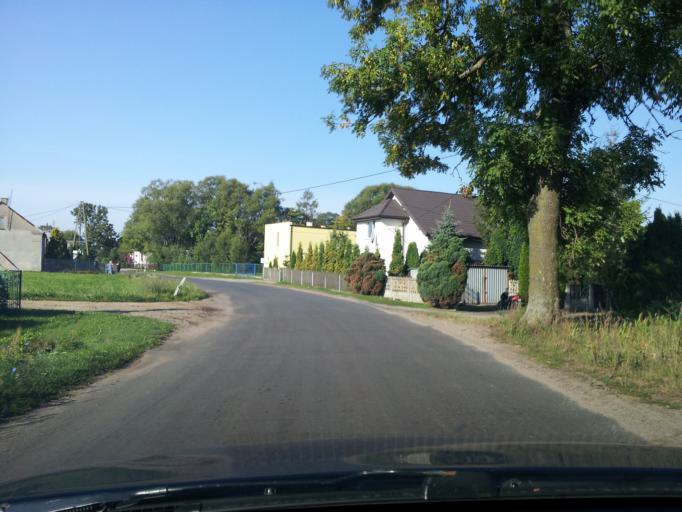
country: PL
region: Kujawsko-Pomorskie
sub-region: Powiat brodnicki
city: Swiedziebnia
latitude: 53.0912
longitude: 19.5190
